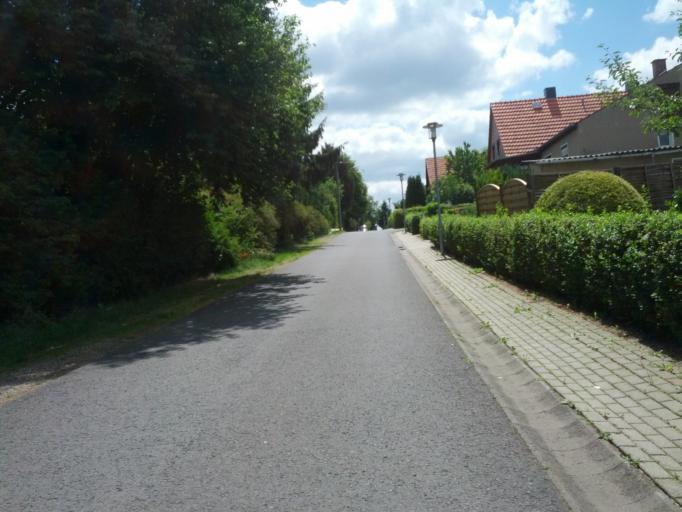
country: DE
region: Thuringia
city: Bischofroda
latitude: 51.0059
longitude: 10.3610
